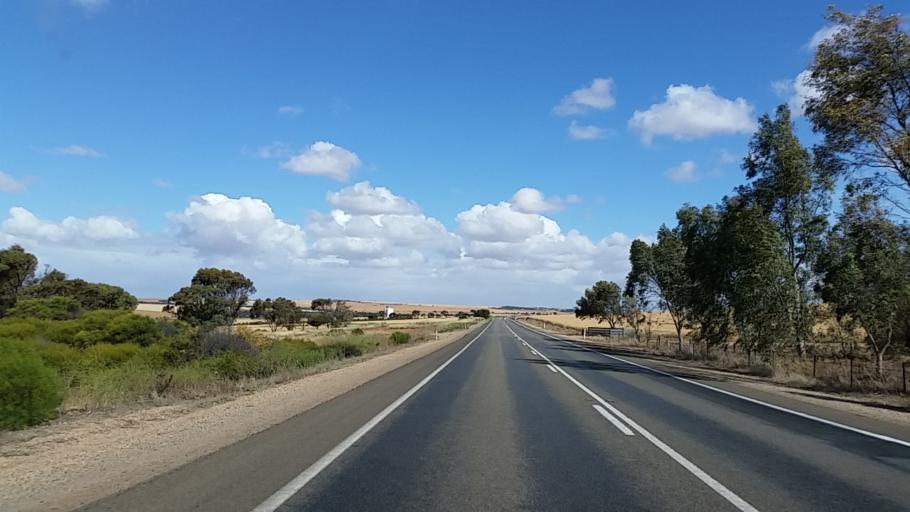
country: AU
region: South Australia
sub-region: Wakefield
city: Balaklava
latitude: -33.9887
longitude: 138.2112
